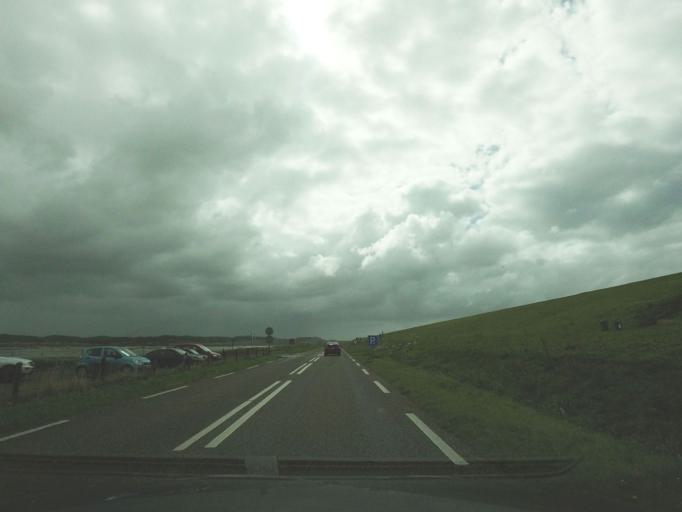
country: NL
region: North Holland
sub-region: Gemeente Bergen
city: Egmond aan Zee
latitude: 52.7400
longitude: 4.6454
